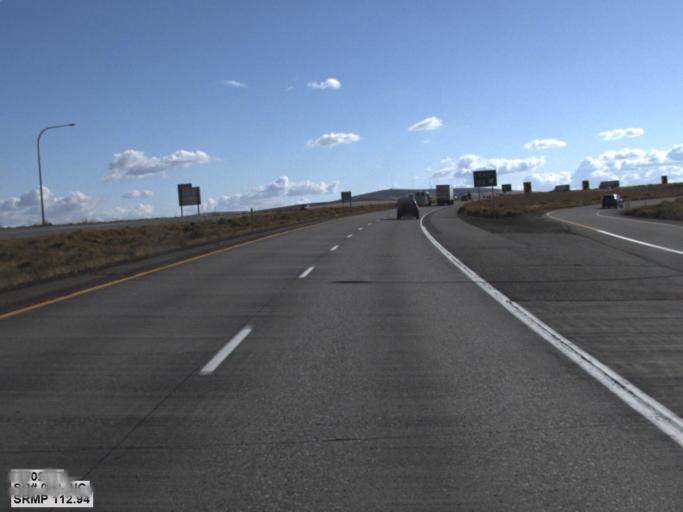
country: US
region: Washington
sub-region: Benton County
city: Kennewick
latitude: 46.1634
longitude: -119.2021
